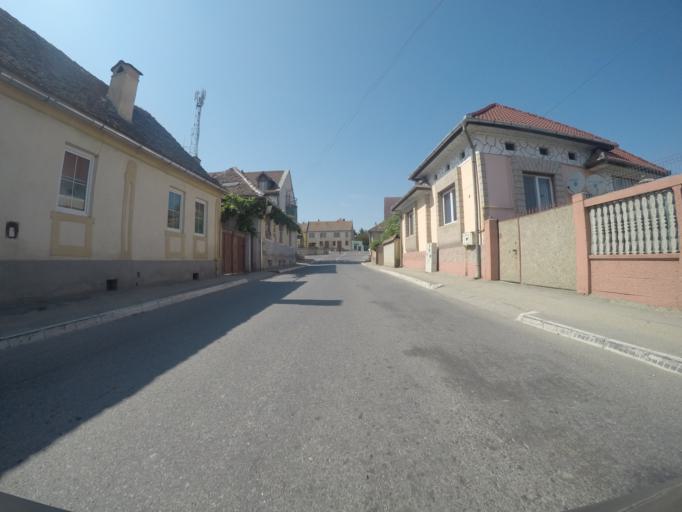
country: RO
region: Sibiu
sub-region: Comuna Avrig
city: Avrig
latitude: 45.7267
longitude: 24.3768
